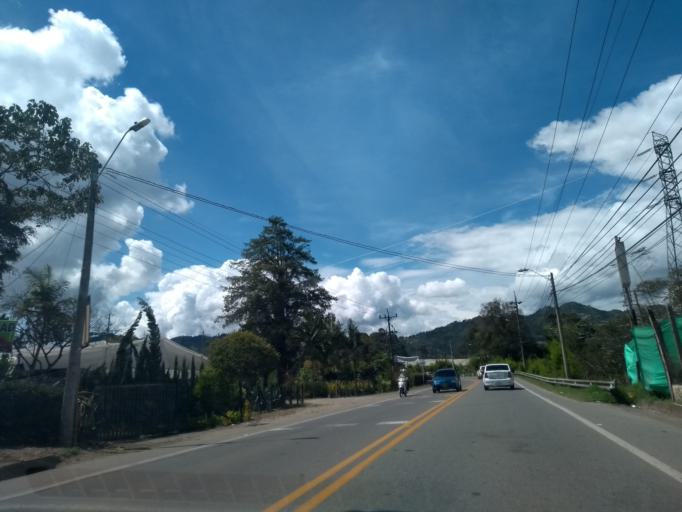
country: CO
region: Antioquia
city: La Ceja
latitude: 6.0392
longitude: -75.4156
